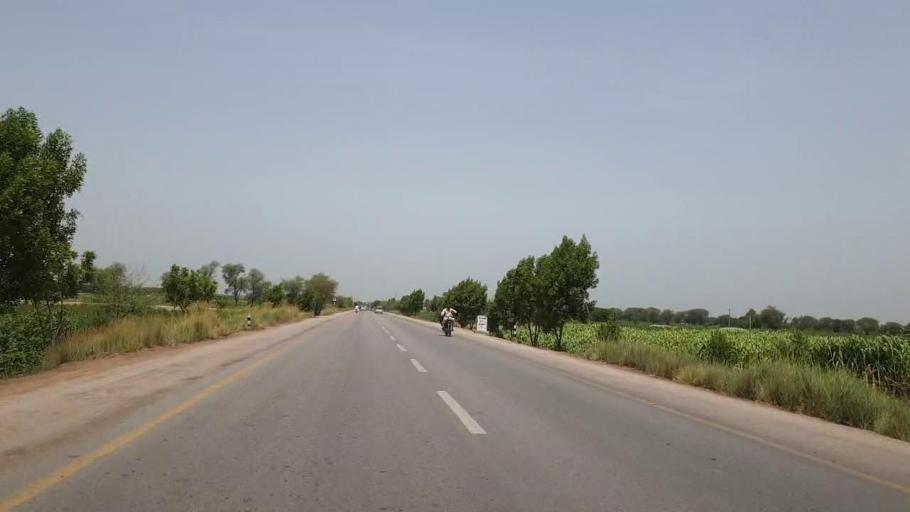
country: PK
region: Sindh
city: Nawabshah
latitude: 26.2348
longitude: 68.4792
